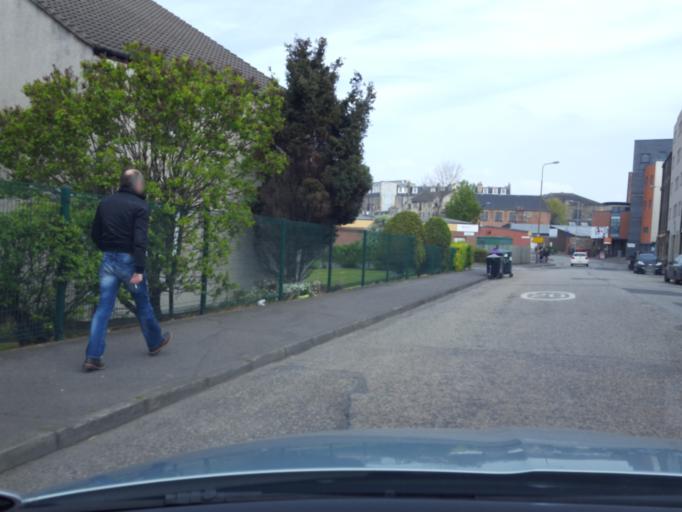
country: GB
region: Scotland
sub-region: Edinburgh
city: Edinburgh
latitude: 55.9712
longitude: -3.1782
